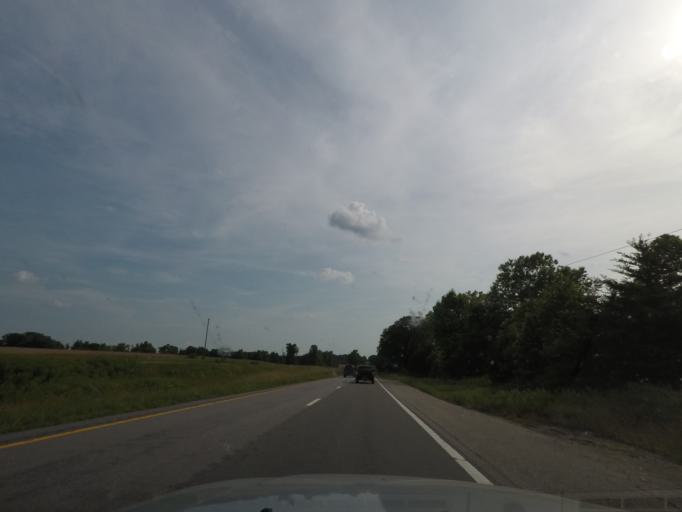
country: US
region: Virginia
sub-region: Mecklenburg County
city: Chase City
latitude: 36.8908
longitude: -78.5490
